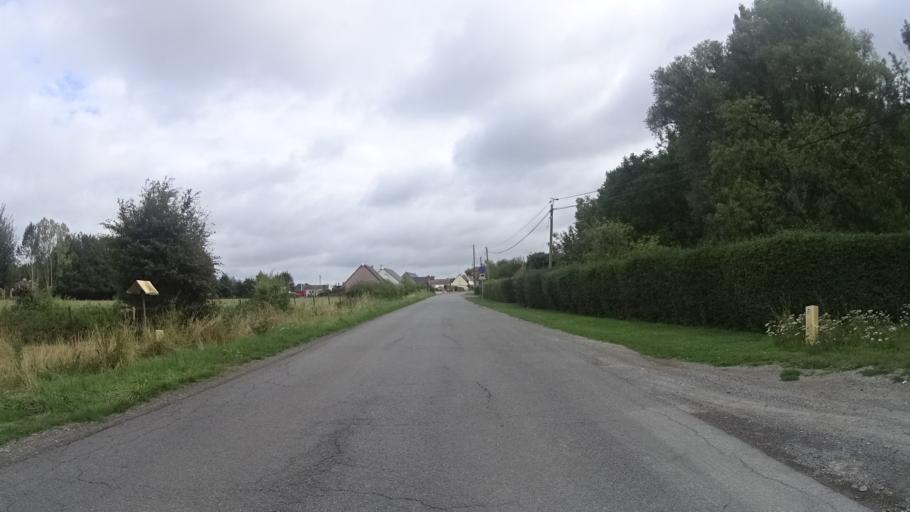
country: FR
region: Picardie
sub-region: Departement de l'Aisne
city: Boue
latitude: 50.0037
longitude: 3.6916
